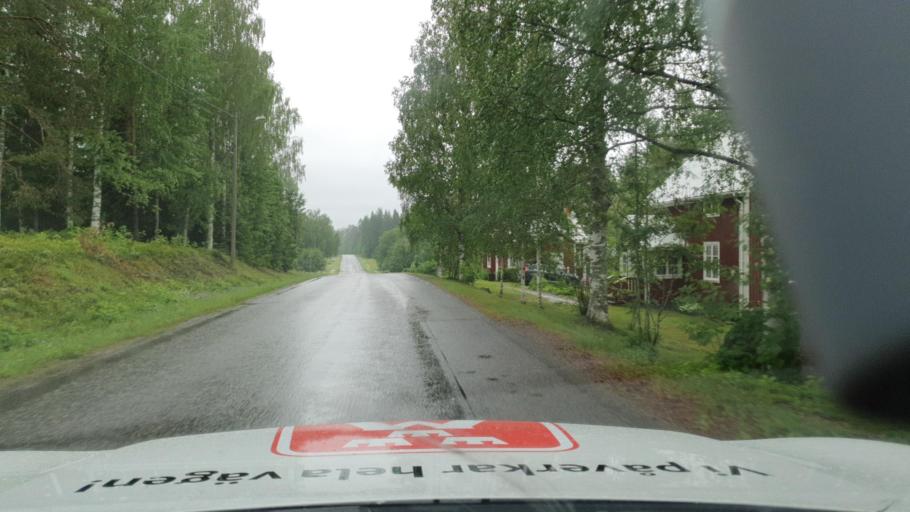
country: SE
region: Vaesterbotten
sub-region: Nordmalings Kommun
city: Nordmaling
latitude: 63.8034
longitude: 19.5043
